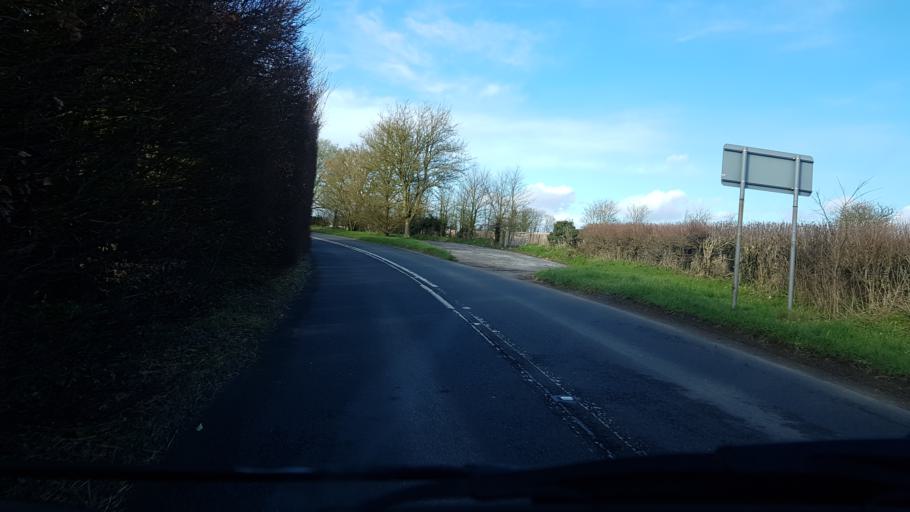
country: GB
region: England
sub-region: Wiltshire
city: Avebury
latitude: 51.4485
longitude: -1.8557
